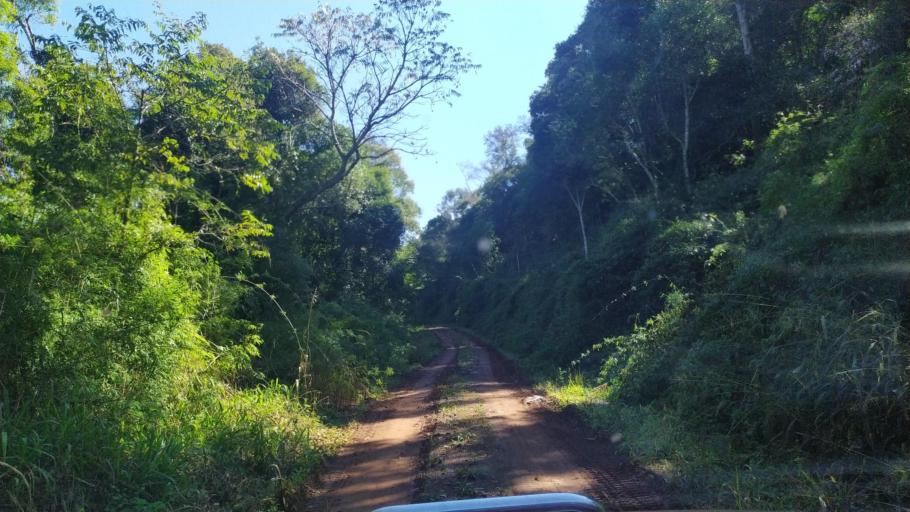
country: AR
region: Misiones
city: El Alcazar
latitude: -26.7558
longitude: -54.5952
